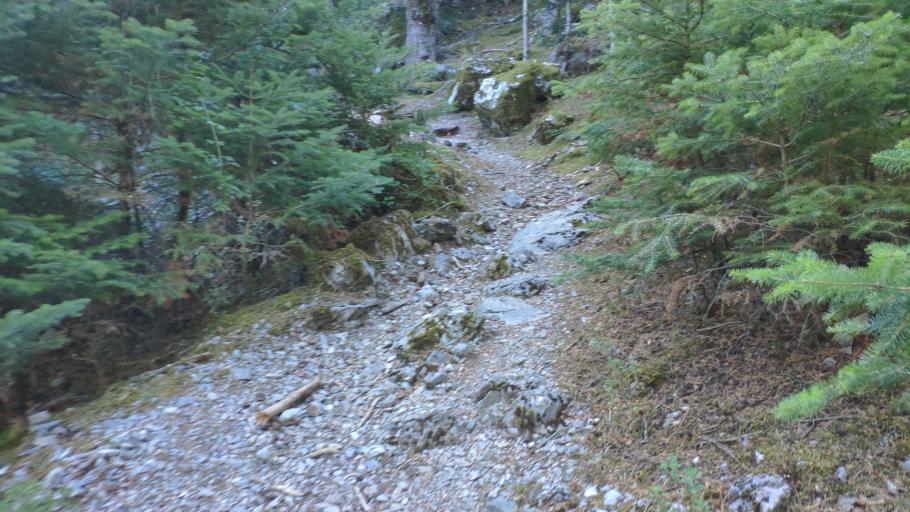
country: GR
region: Peloponnese
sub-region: Nomos Lakonias
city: Kariai
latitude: 37.1739
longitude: 22.5995
